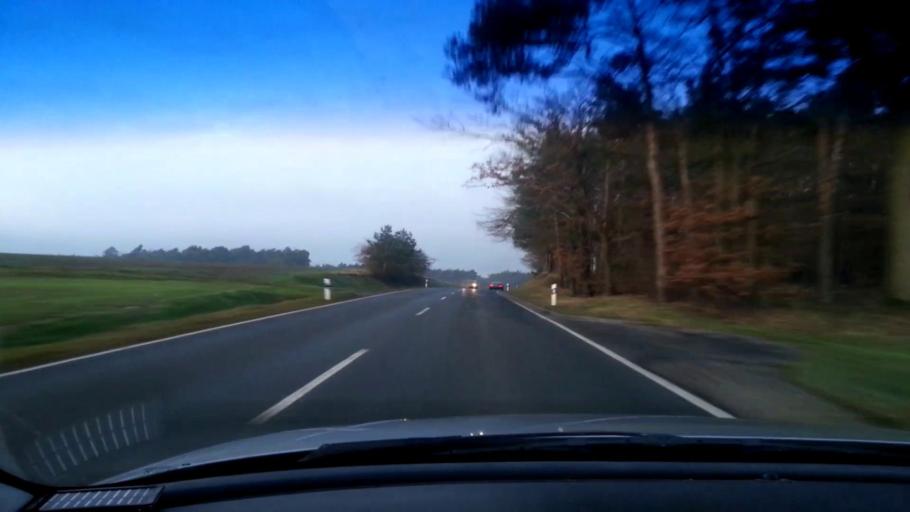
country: DE
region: Bavaria
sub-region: Upper Franconia
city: Pommersfelden
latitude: 49.7940
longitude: 10.8263
